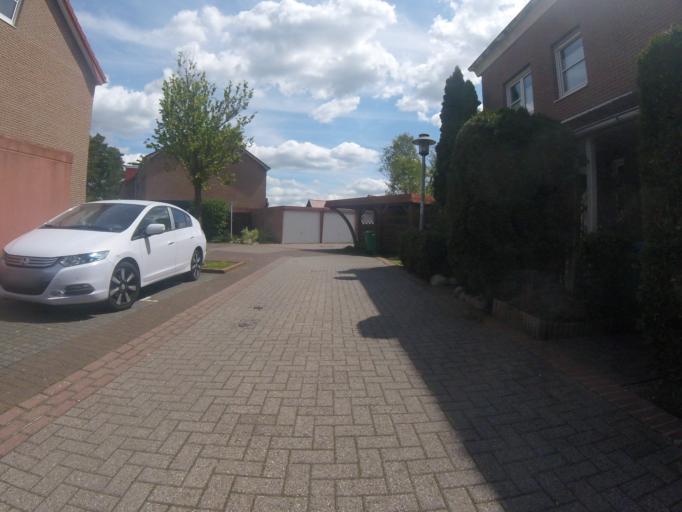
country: DE
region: Brandenburg
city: Konigs Wusterhausen
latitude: 52.2974
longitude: 13.6063
